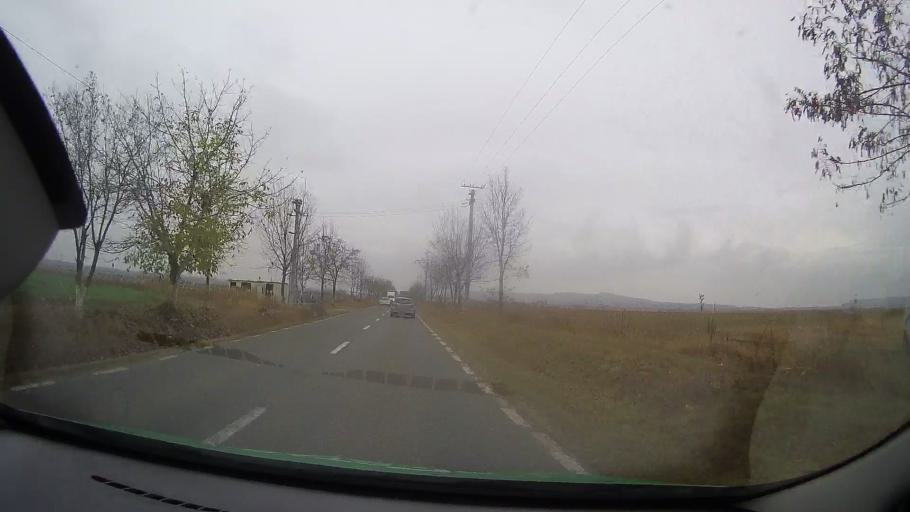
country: RO
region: Prahova
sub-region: Oras Baicoi
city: Liliesti
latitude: 45.0090
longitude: 25.8842
